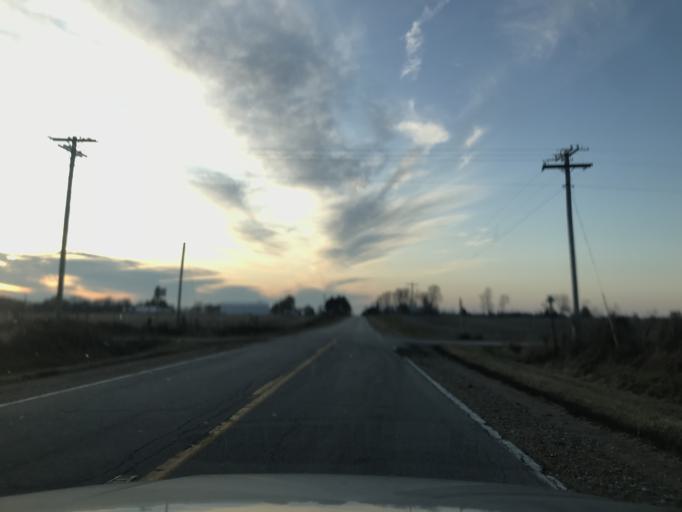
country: US
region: Illinois
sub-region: Warren County
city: Monmouth
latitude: 41.0249
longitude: -90.7650
